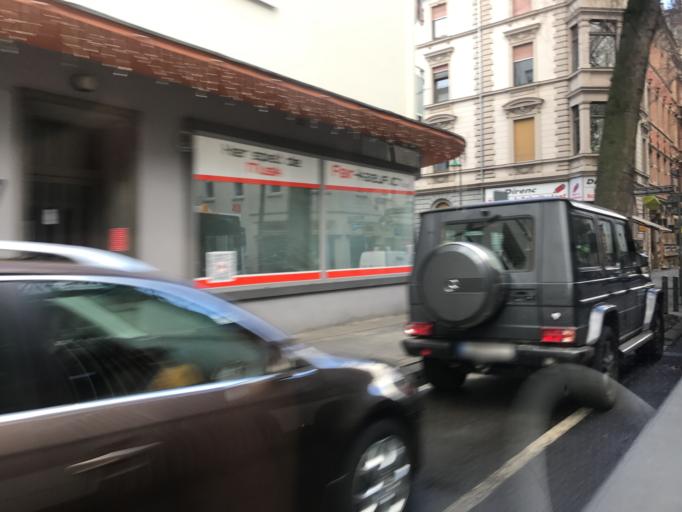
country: DE
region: Hesse
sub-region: Regierungsbezirk Darmstadt
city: Wiesbaden
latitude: 50.0728
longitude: 8.2389
